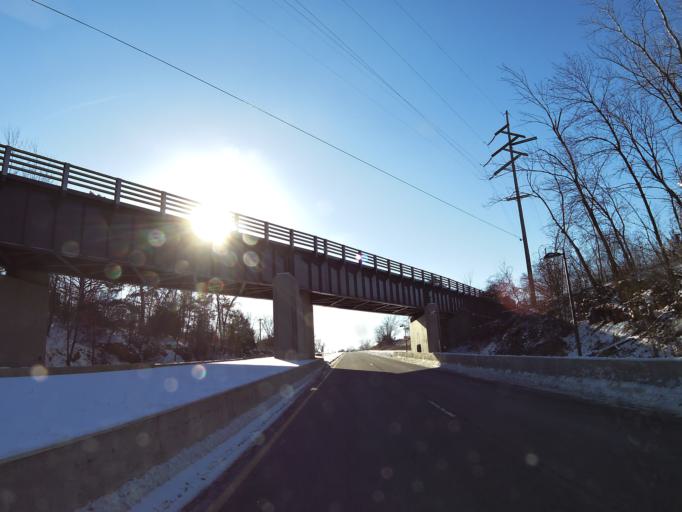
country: US
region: Minnesota
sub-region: Scott County
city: Shakopee
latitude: 44.7956
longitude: -93.5440
